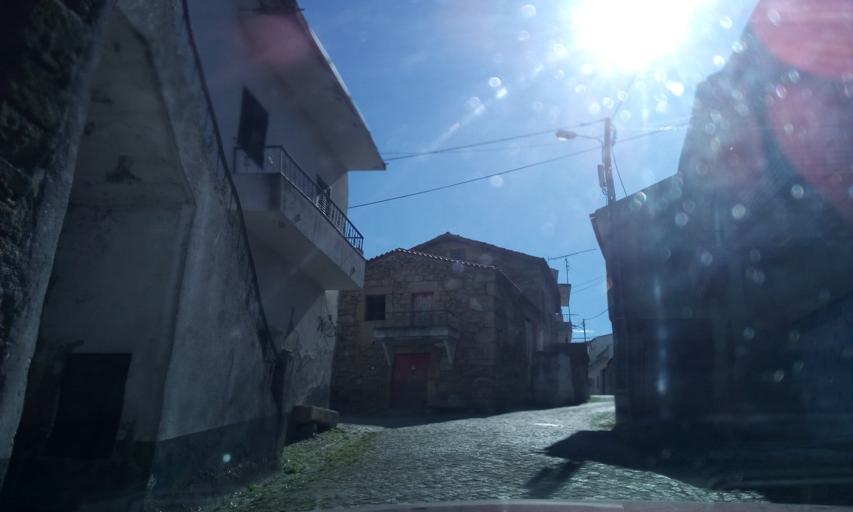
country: PT
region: Guarda
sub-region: Guarda
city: Guarda
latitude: 40.5867
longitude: -7.2878
